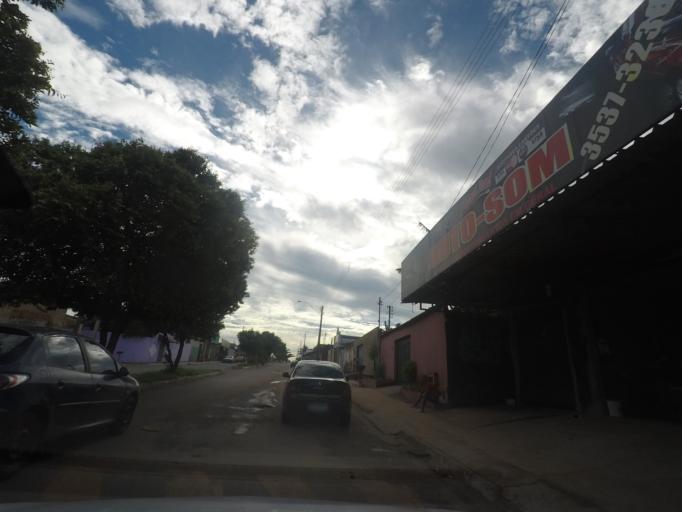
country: BR
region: Goias
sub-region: Aparecida De Goiania
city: Aparecida de Goiania
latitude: -16.8168
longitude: -49.3183
